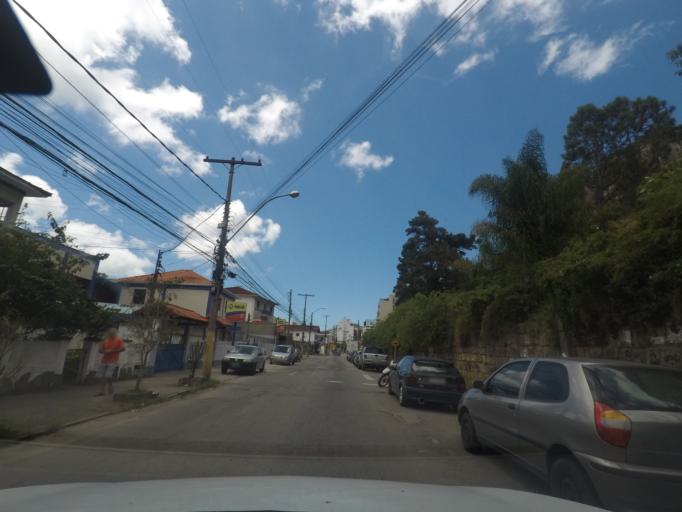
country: BR
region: Rio de Janeiro
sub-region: Teresopolis
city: Teresopolis
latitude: -22.4064
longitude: -42.9672
